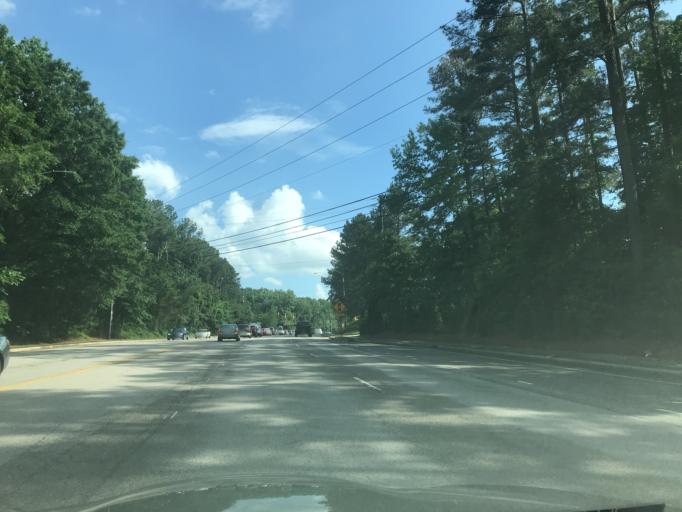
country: US
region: North Carolina
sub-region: Wake County
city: West Raleigh
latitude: 35.8669
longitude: -78.6381
